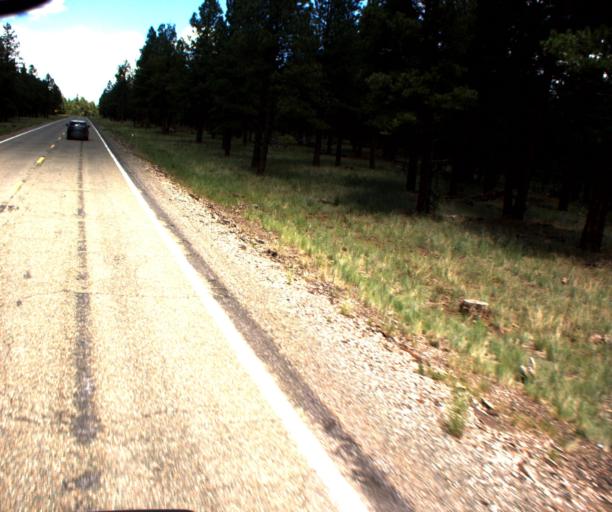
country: US
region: Arizona
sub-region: Coconino County
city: Parks
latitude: 35.3595
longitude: -111.7910
